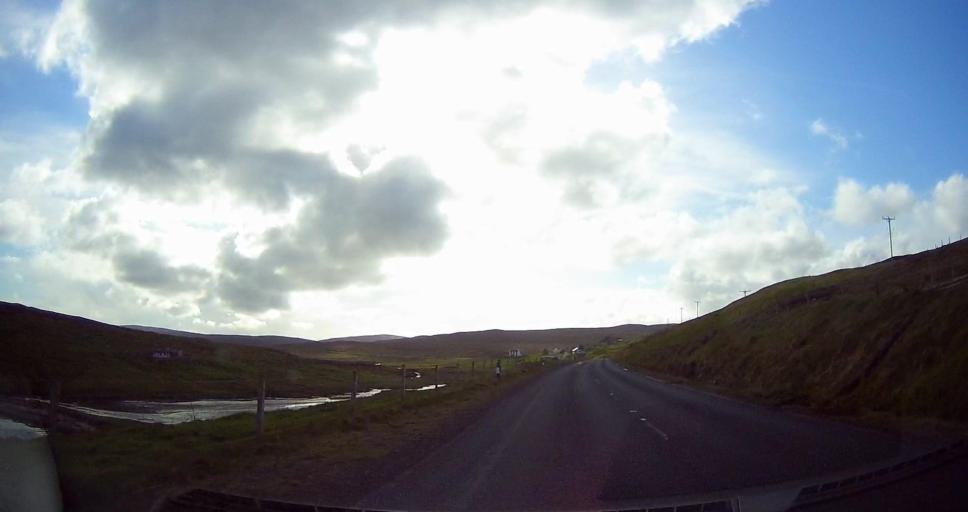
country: GB
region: Scotland
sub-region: Shetland Islands
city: Lerwick
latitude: 60.3528
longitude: -1.1835
